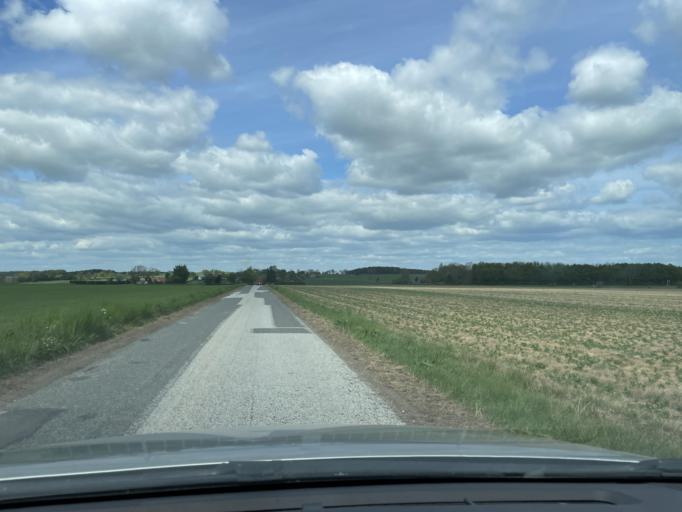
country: DK
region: Central Jutland
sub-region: Odder Kommune
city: Odder
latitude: 55.9058
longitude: 10.1198
